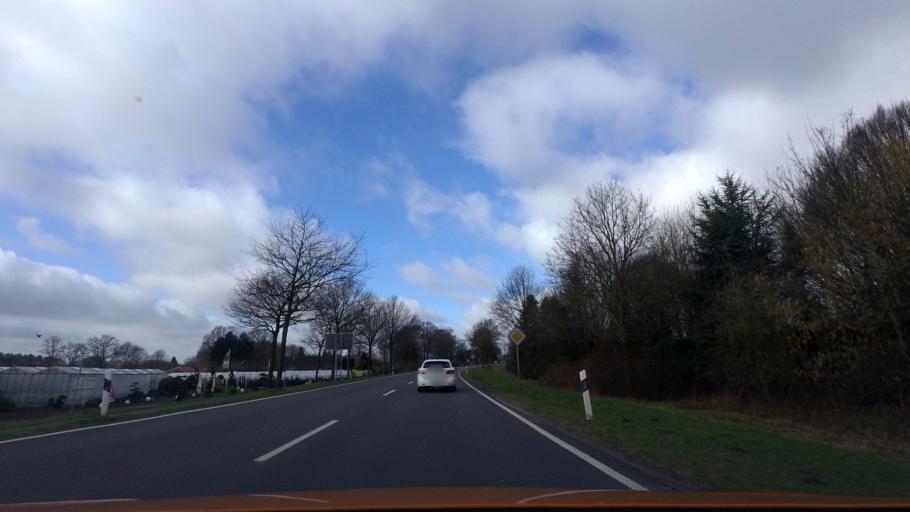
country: DE
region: Lower Saxony
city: Buehren
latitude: 52.8097
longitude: 8.2213
